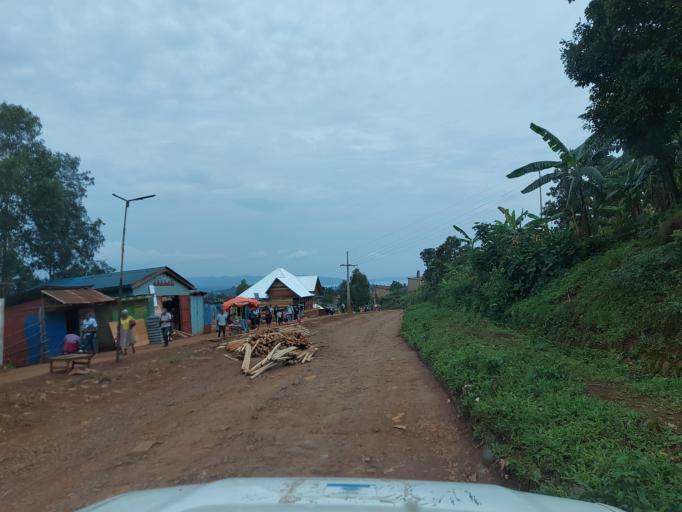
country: CD
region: South Kivu
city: Bukavu
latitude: -2.4800
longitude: 28.8216
